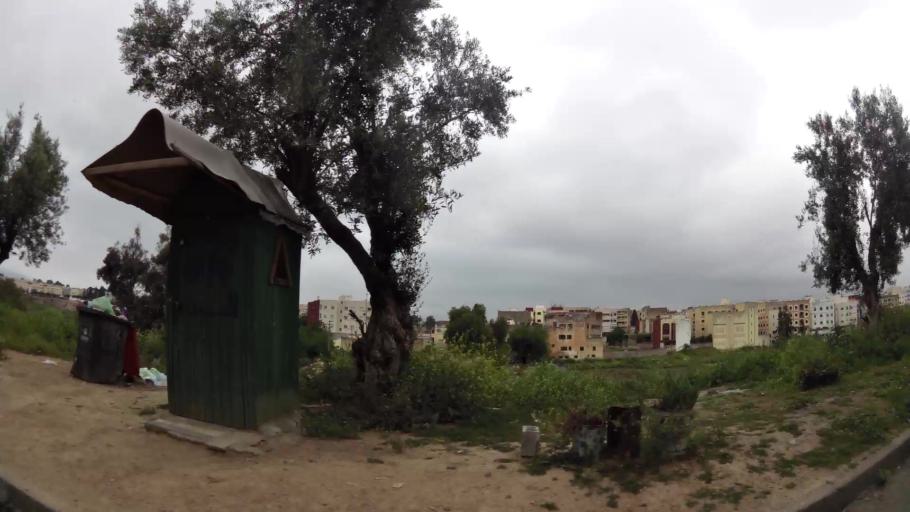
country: MA
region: Fes-Boulemane
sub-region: Fes
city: Fes
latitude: 34.0351
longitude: -4.9930
